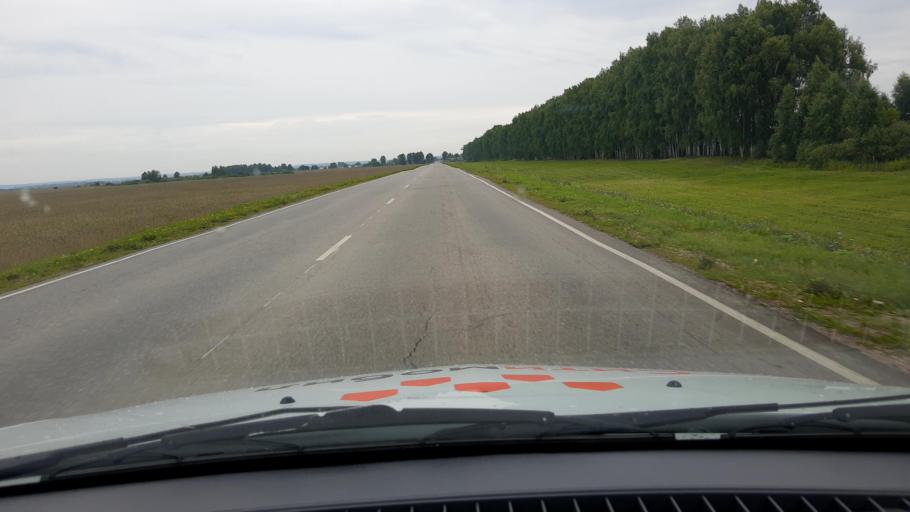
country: RU
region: Bashkortostan
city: Krasnaya Gorka
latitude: 55.1057
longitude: 56.6289
